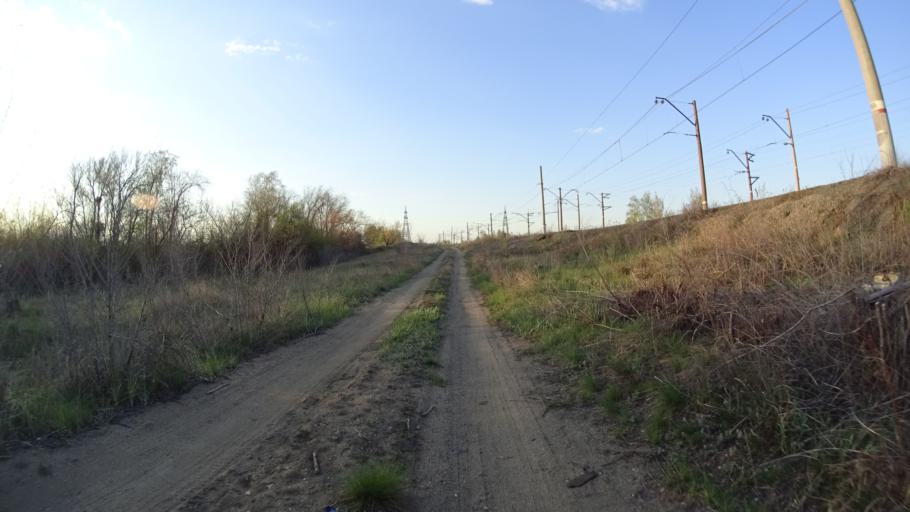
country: RU
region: Chelyabinsk
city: Troitsk
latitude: 54.0586
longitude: 61.6134
